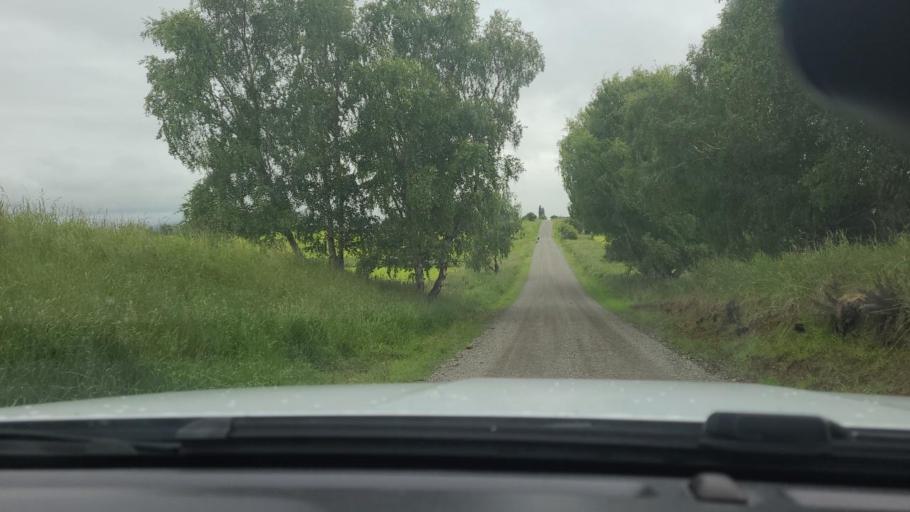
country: NZ
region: Southland
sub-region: Southland District
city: Riverton
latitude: -46.0658
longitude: 168.0523
